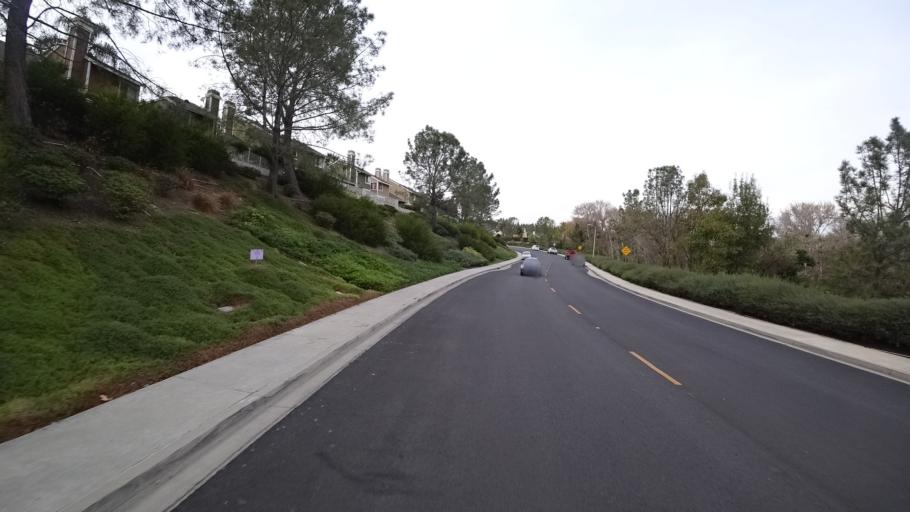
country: US
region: California
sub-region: Orange County
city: Laguna Hills
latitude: 33.5909
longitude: -117.7150
